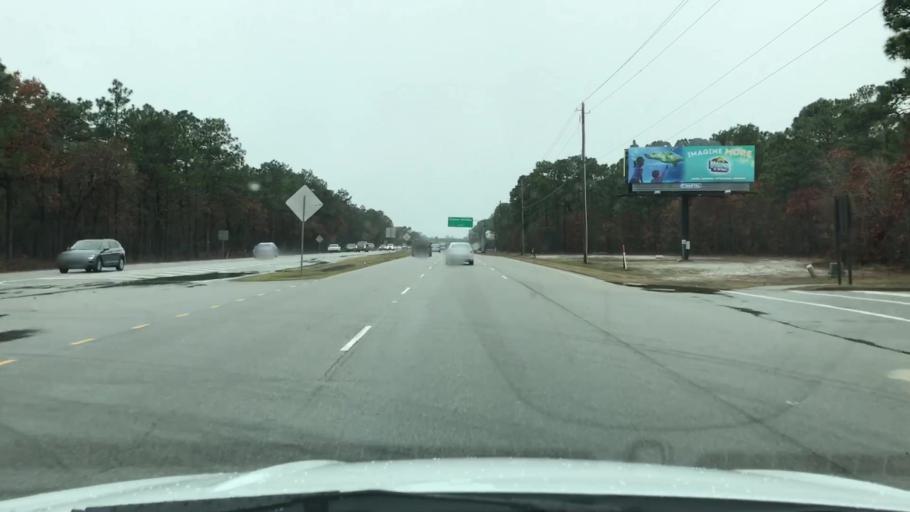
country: US
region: South Carolina
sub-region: Horry County
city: Myrtle Beach
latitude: 33.7507
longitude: -78.8320
